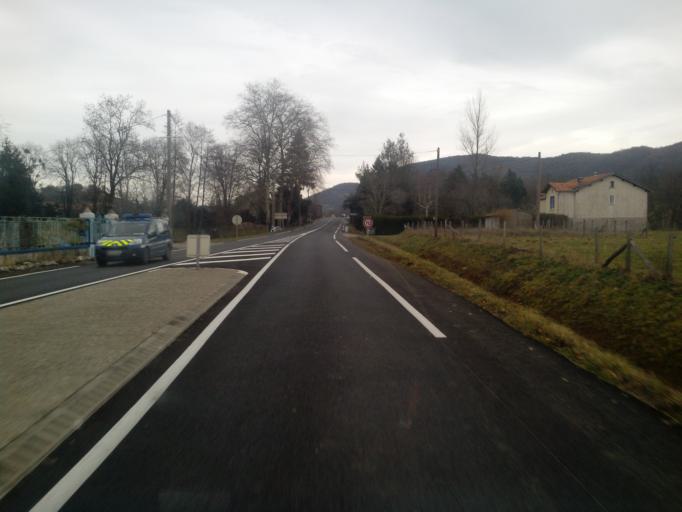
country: FR
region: Midi-Pyrenees
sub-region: Departement de l'Ariege
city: Foix
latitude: 43.0083
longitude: 1.4612
